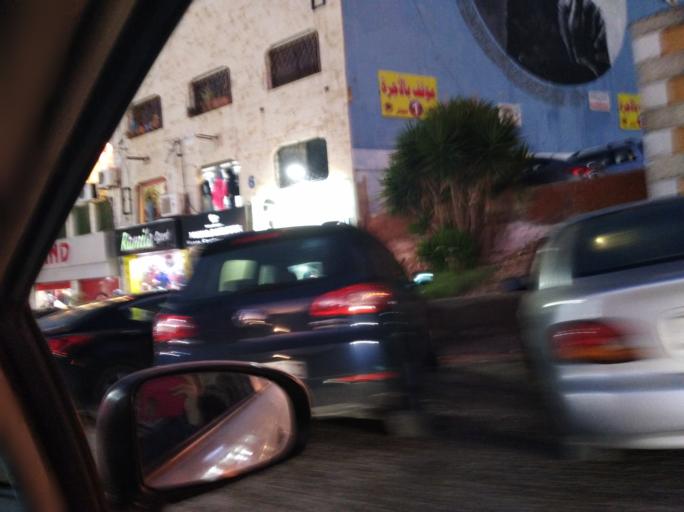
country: JO
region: Amman
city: Wadi as Sir
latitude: 31.9570
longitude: 35.8653
